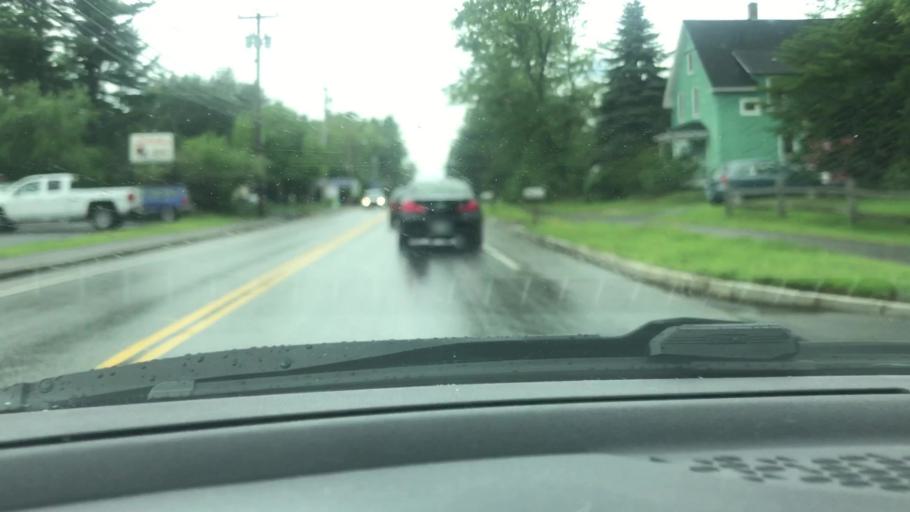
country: US
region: New Hampshire
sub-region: Merrimack County
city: East Concord
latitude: 43.2521
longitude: -71.5744
